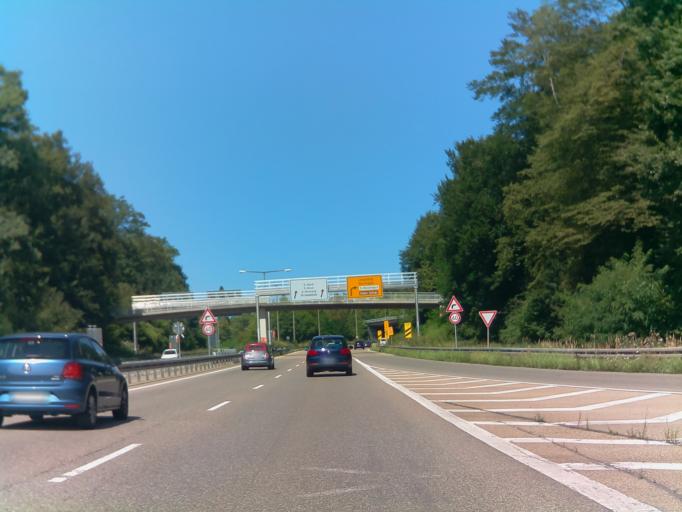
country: DE
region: Baden-Wuerttemberg
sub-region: Regierungsbezirk Stuttgart
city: Stuttgart Feuerbach
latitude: 48.7613
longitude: 9.1165
